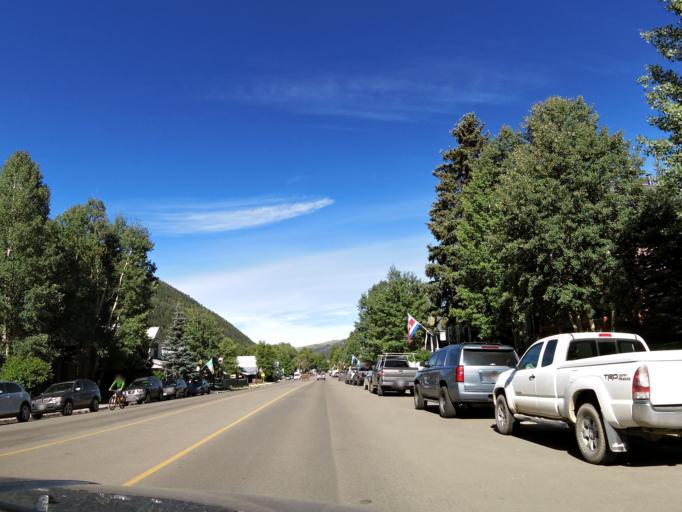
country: US
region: Colorado
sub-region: San Miguel County
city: Telluride
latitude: 37.9381
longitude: -107.8142
